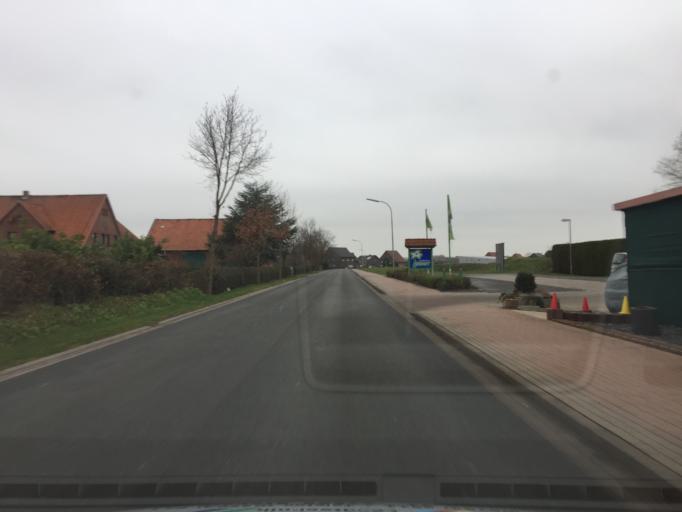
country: DE
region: Lower Saxony
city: Niedernwohren
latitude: 52.3437
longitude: 9.1426
